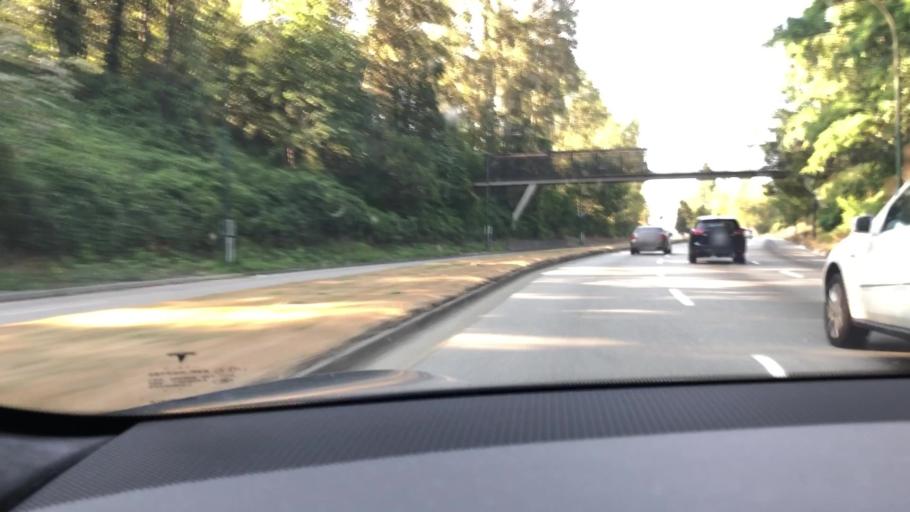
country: CA
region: British Columbia
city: Burnaby
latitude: 49.2104
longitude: -123.0239
